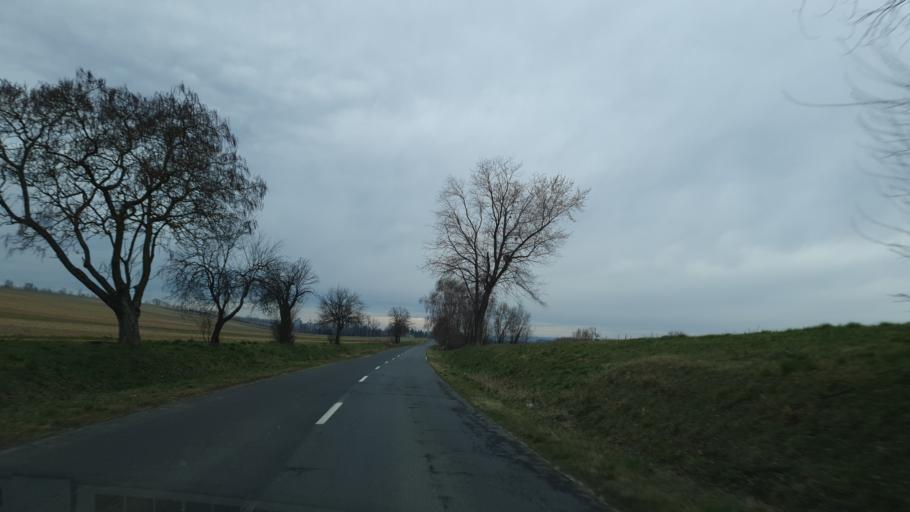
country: HU
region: Zala
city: Sarmellek
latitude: 46.6852
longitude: 17.1086
